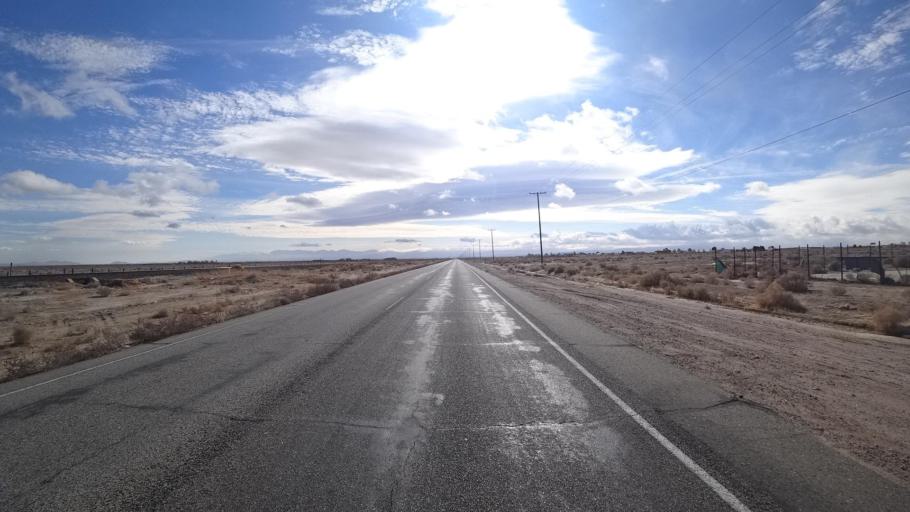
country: US
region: California
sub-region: Kern County
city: Rosamond
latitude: 34.8320
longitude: -118.1579
